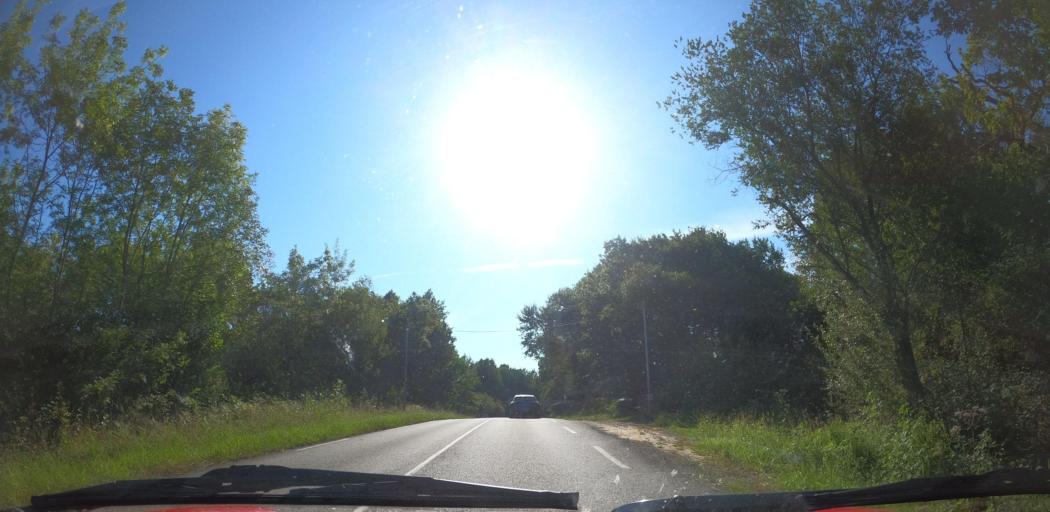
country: FR
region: Aquitaine
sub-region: Departement des Pyrenees-Atlantiques
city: Saint-Pee-sur-Nivelle
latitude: 43.3820
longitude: -1.5408
